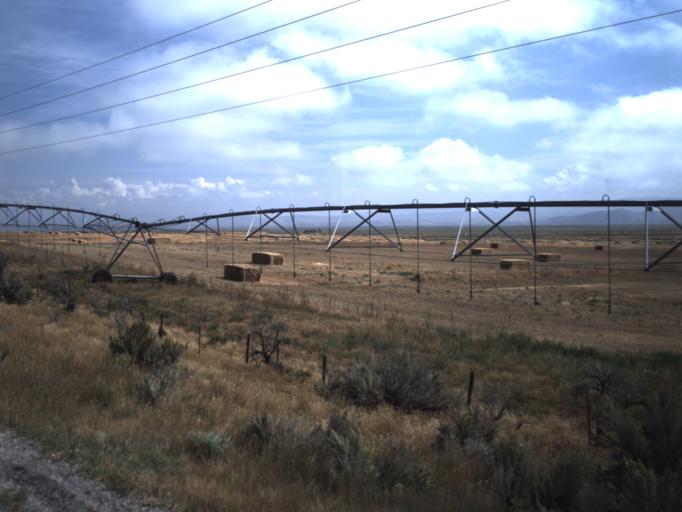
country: US
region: Utah
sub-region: Rich County
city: Randolph
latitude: 41.7502
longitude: -111.1446
